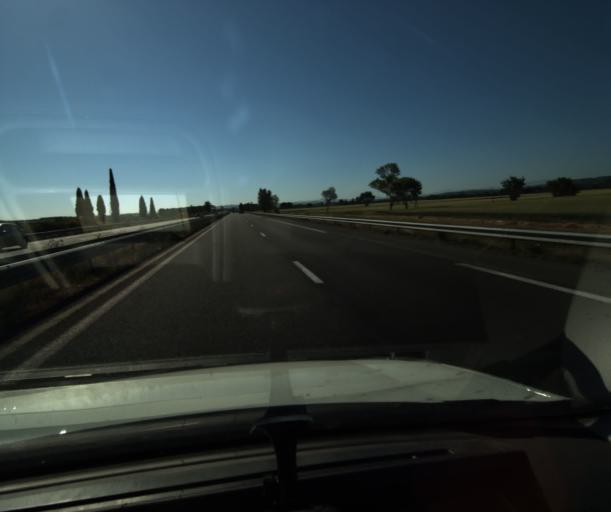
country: FR
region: Languedoc-Roussillon
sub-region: Departement de l'Aude
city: Saint-Martin-Lalande
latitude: 43.2634
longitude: 2.0184
